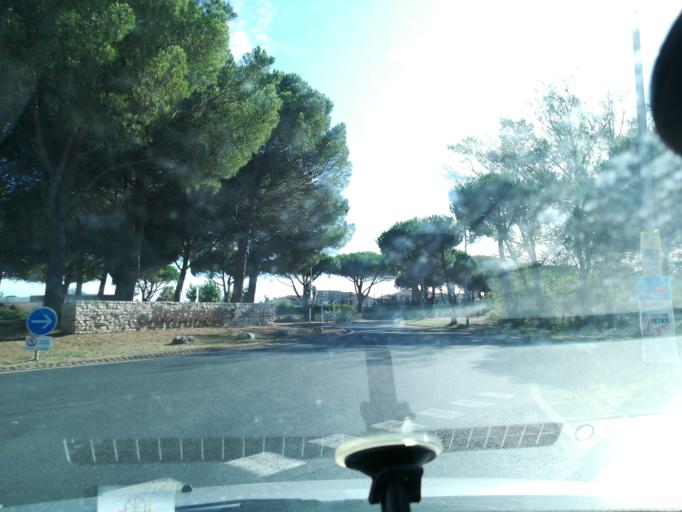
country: FR
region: Languedoc-Roussillon
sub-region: Departement de l'Herault
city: Portiragnes
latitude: 43.2838
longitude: 3.3625
